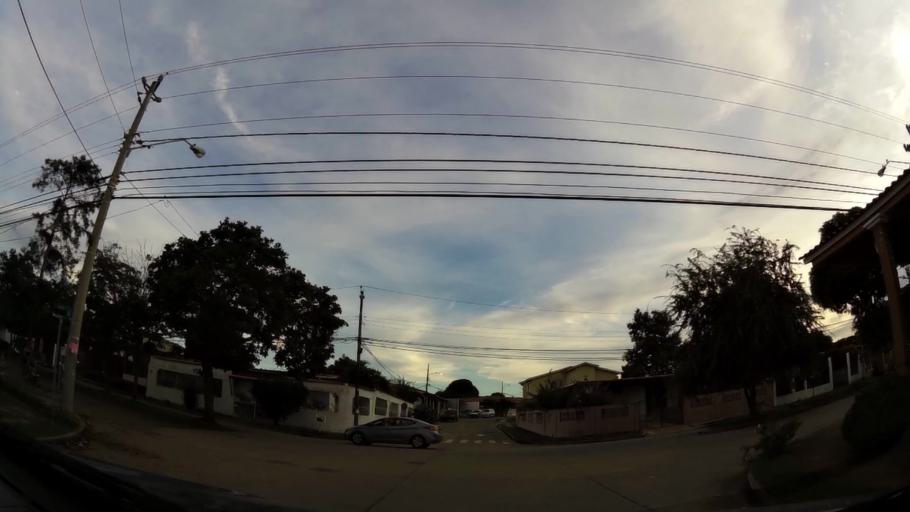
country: PA
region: Panama
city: La Chorrera
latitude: 8.8683
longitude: -79.7637
